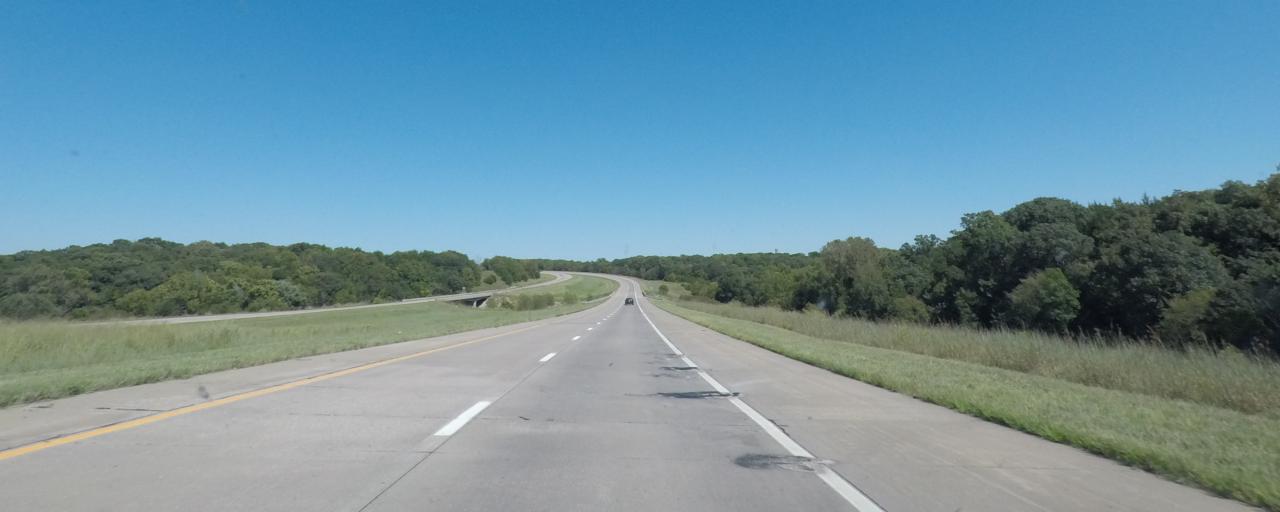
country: US
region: Kansas
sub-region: Osage County
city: Lyndon
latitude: 38.4719
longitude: -95.5240
